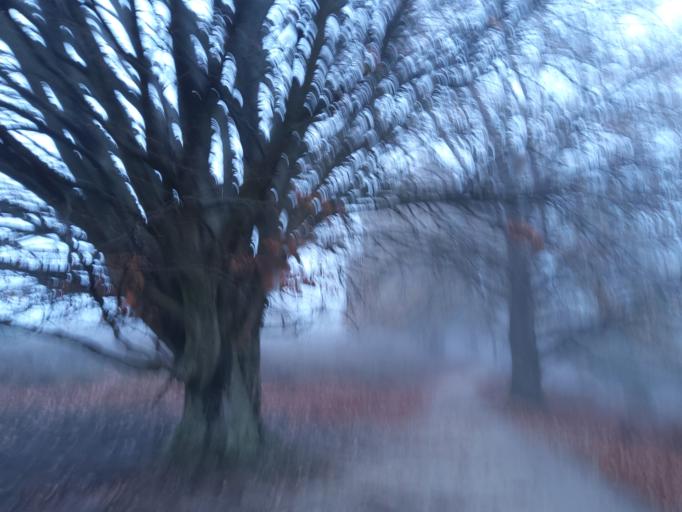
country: NL
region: Gelderland
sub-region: Gemeente Rheden
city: Rheden
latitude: 52.0272
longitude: 6.0167
